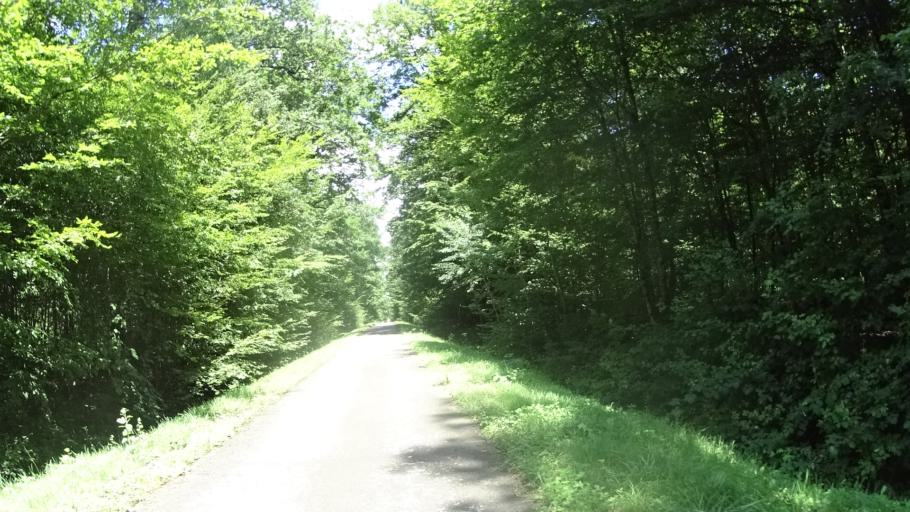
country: FR
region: Champagne-Ardenne
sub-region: Departement de la Haute-Marne
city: Montier-en-Der
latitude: 48.5271
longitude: 4.7703
